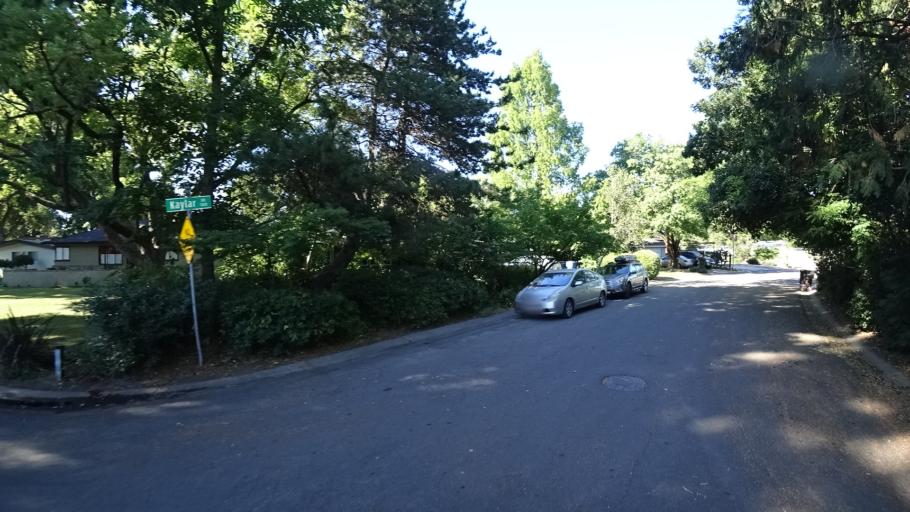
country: US
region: California
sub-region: Yolo County
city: West Sacramento
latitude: 38.5269
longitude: -121.5126
